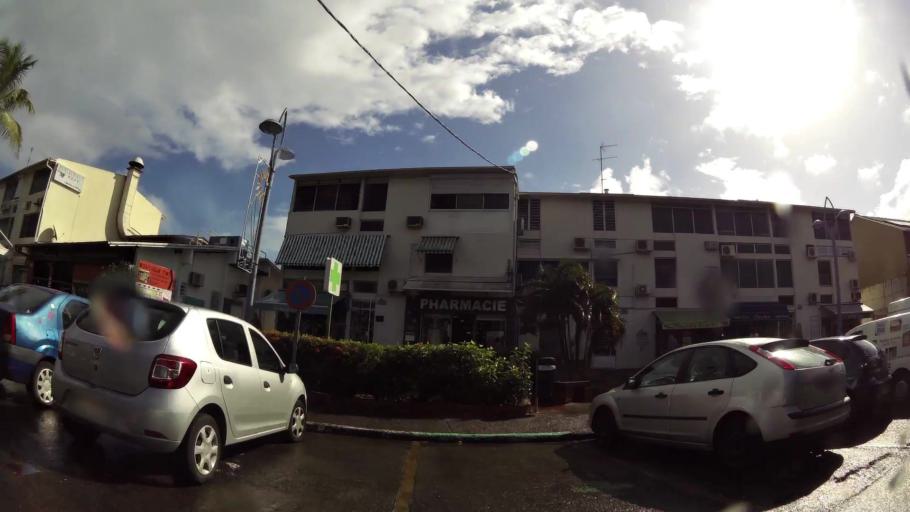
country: MQ
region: Martinique
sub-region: Martinique
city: Les Trois-Ilets
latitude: 14.5570
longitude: -61.0518
